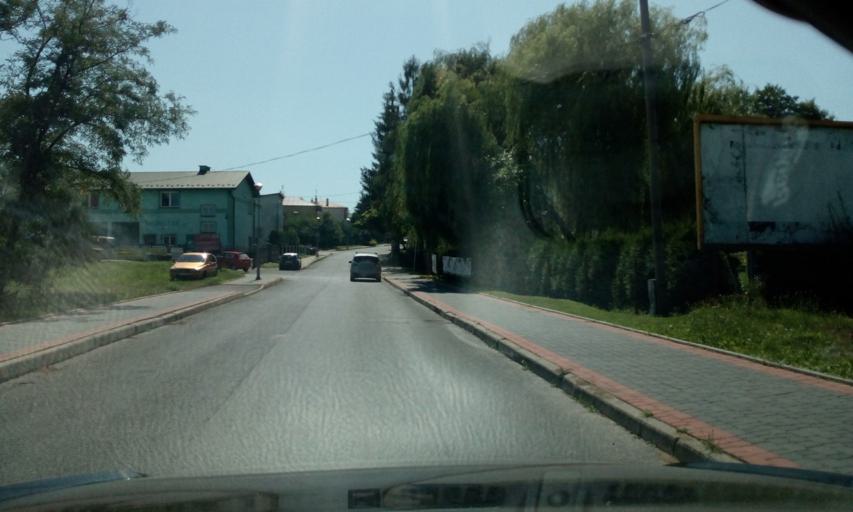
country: PL
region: Subcarpathian Voivodeship
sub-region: Powiat lancucki
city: Lancut
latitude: 50.0586
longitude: 22.2350
